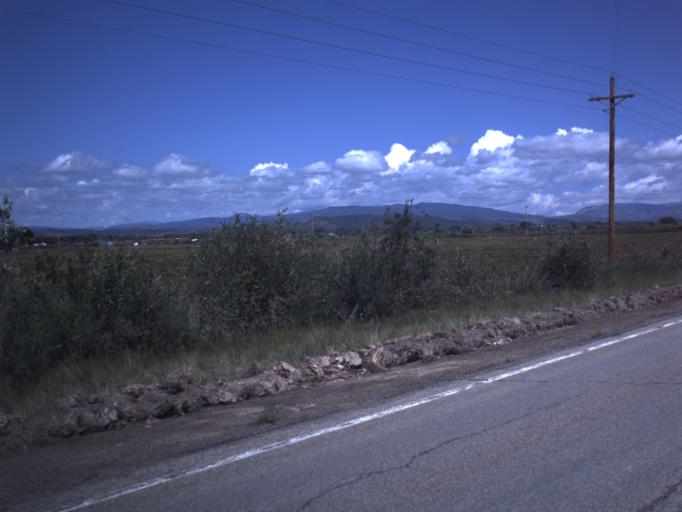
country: US
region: Utah
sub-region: Duchesne County
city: Roosevelt
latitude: 40.4154
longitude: -110.0299
